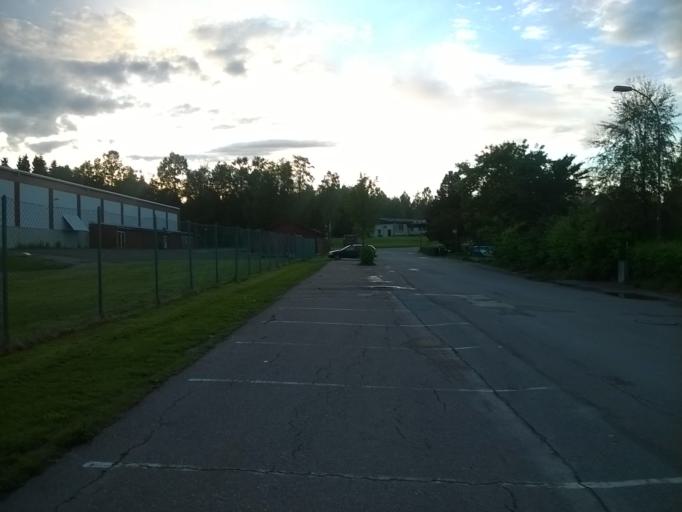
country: SE
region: Dalarna
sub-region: Saters Kommun
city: Saeter
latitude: 60.3503
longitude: 15.7406
